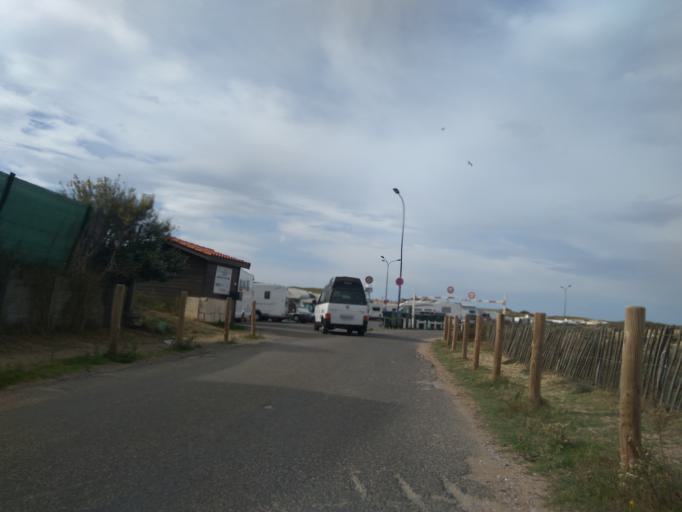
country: FR
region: Aquitaine
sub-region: Departement des Landes
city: Capbreton
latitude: 43.6355
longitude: -1.4461
